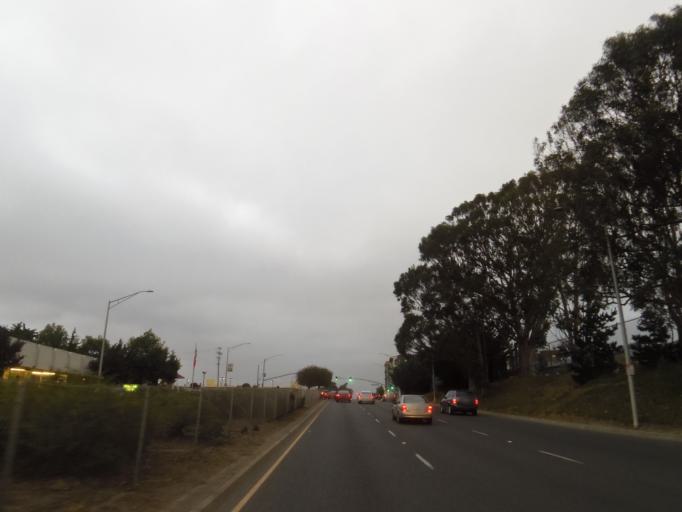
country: US
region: California
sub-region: San Mateo County
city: South San Francisco
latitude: 37.6475
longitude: -122.4287
